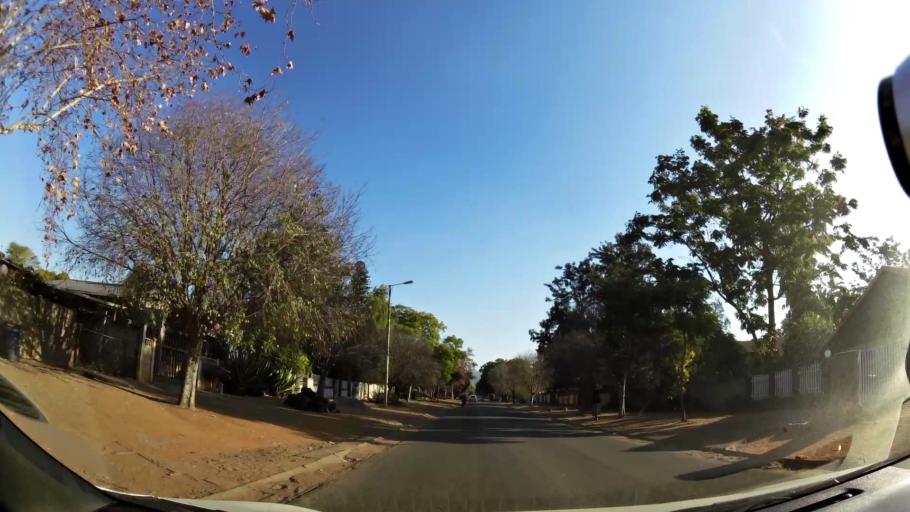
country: ZA
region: North-West
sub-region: Bojanala Platinum District Municipality
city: Rustenburg
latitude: -25.6764
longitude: 27.2356
